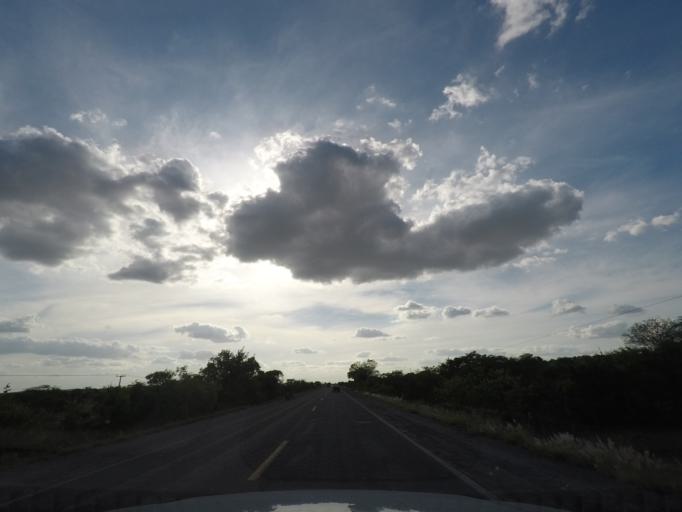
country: BR
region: Bahia
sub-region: Anguera
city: Anguera
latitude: -12.1852
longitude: -39.4784
